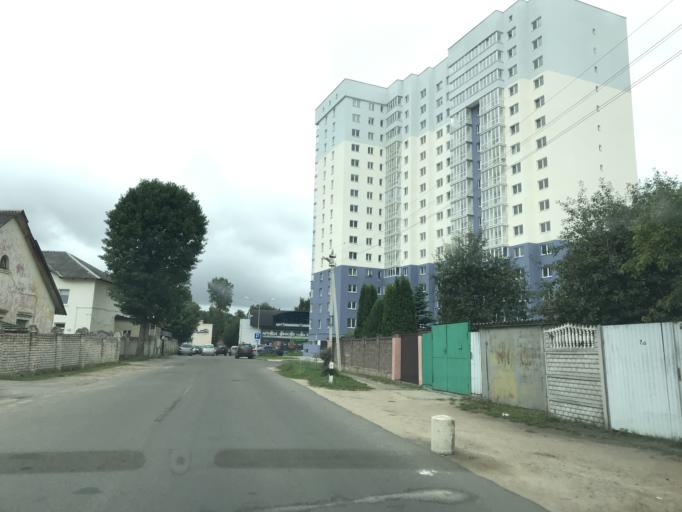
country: BY
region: Minsk
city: Minsk
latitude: 53.9336
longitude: 27.6240
